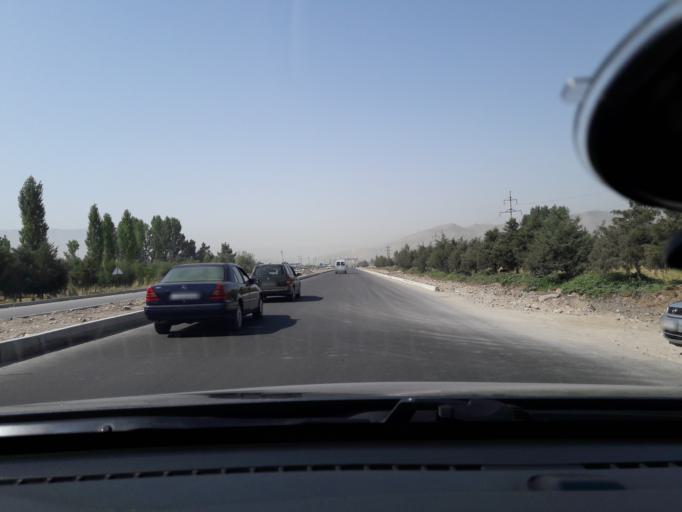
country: TJ
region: Dushanbe
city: Boshkengash
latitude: 38.4811
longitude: 68.7468
